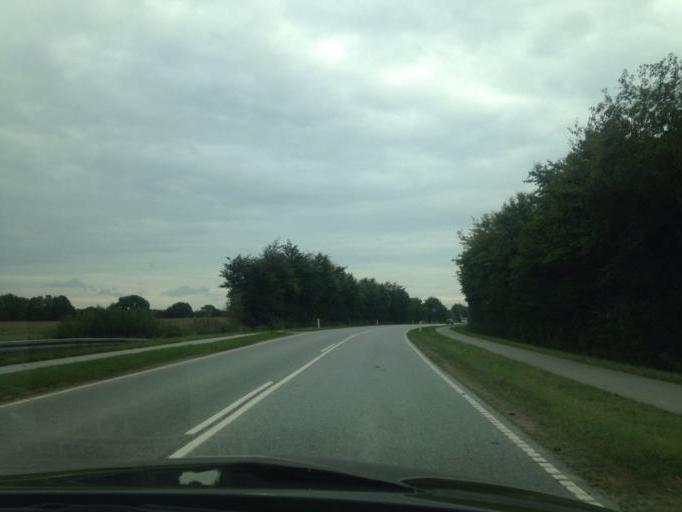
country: DK
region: South Denmark
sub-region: Haderslev Kommune
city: Haderslev
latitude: 55.2466
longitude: 9.4281
